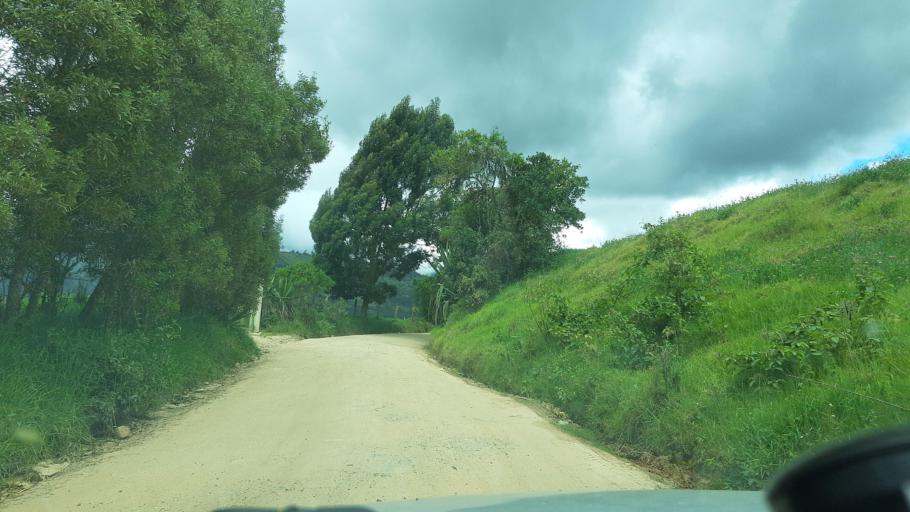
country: CO
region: Cundinamarca
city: Umbita
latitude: 5.2189
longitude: -73.4486
